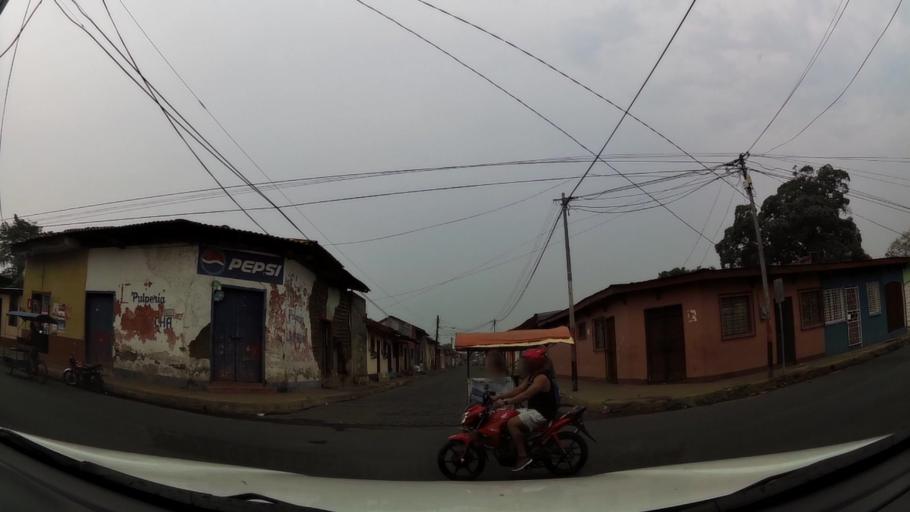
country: NI
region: Leon
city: Leon
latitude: 12.4425
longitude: -86.8785
